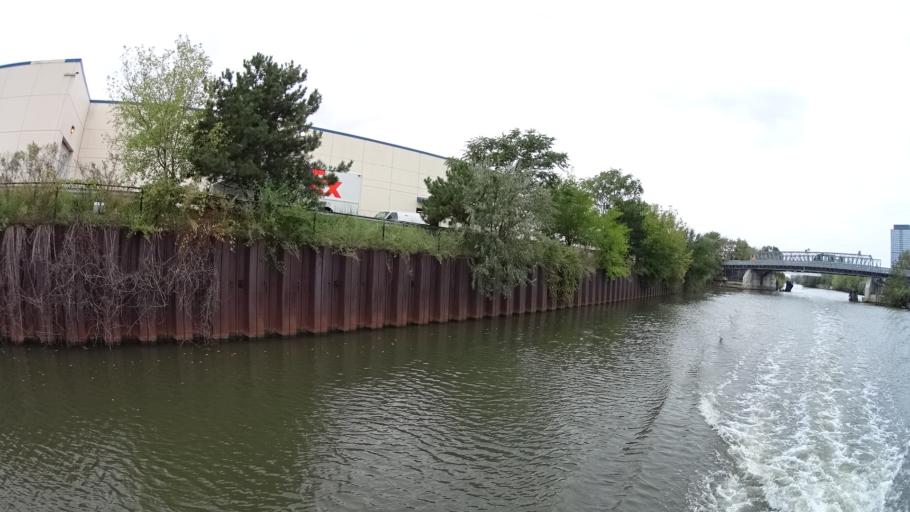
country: US
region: Illinois
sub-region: Cook County
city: Chicago
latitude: 41.9027
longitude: -87.6488
